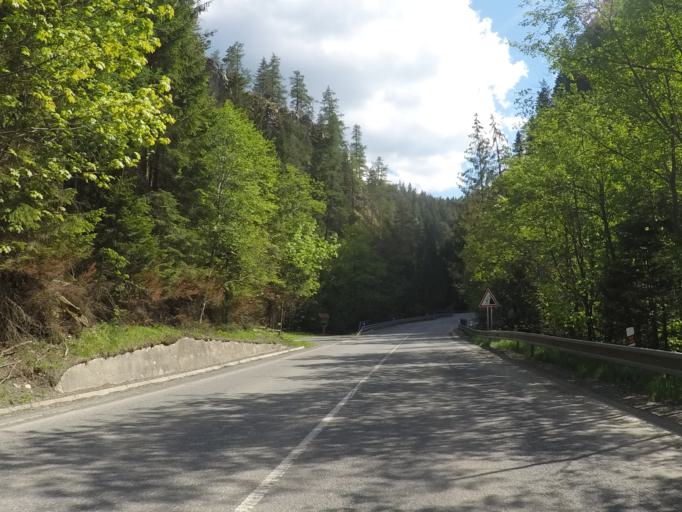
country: SK
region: Presovsky
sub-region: Okres Poprad
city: Poprad
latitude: 48.9336
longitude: 20.2861
